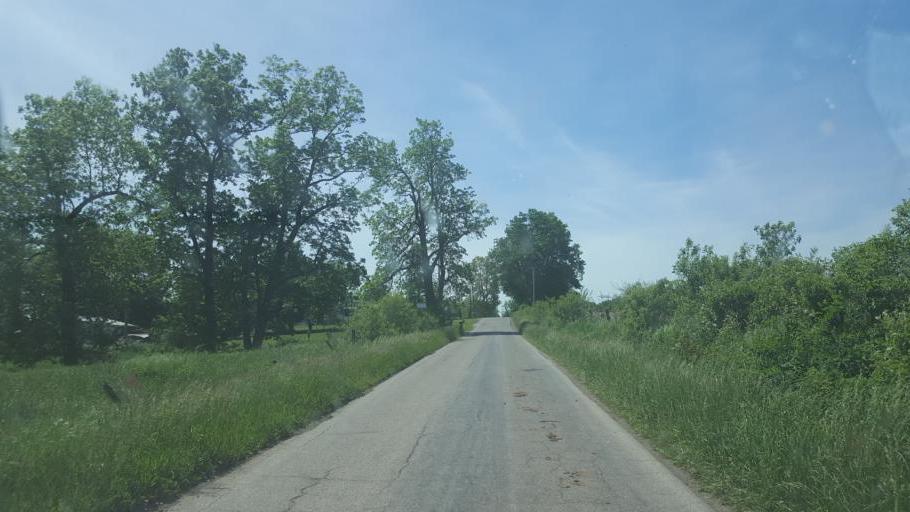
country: US
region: Ohio
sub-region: Knox County
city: Oak Hill
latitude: 40.3247
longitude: -82.2591
